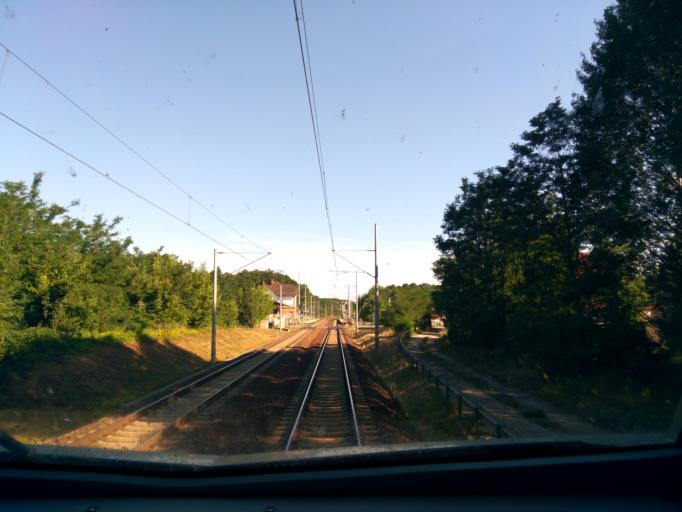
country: DE
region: Brandenburg
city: Gross Koris
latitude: 52.1581
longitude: 13.6516
